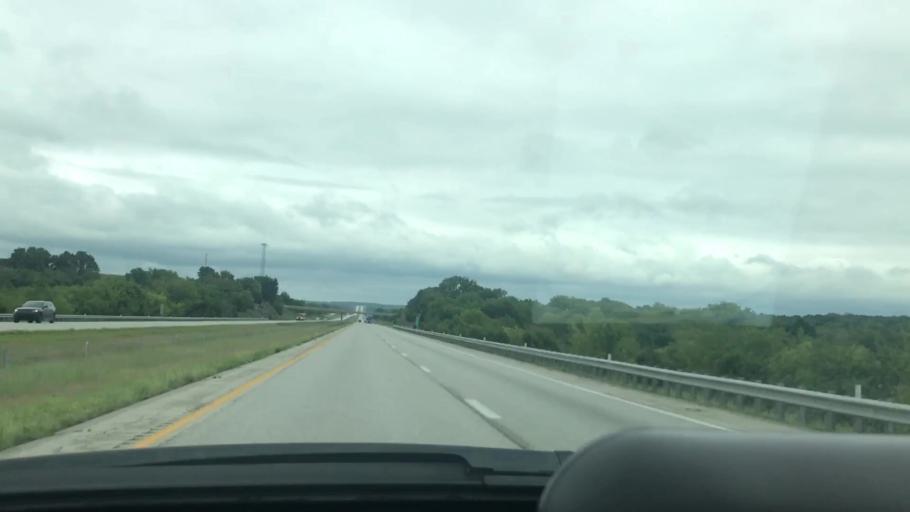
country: US
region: Missouri
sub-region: Lawrence County
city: Mount Vernon
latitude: 37.1521
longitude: -93.7008
